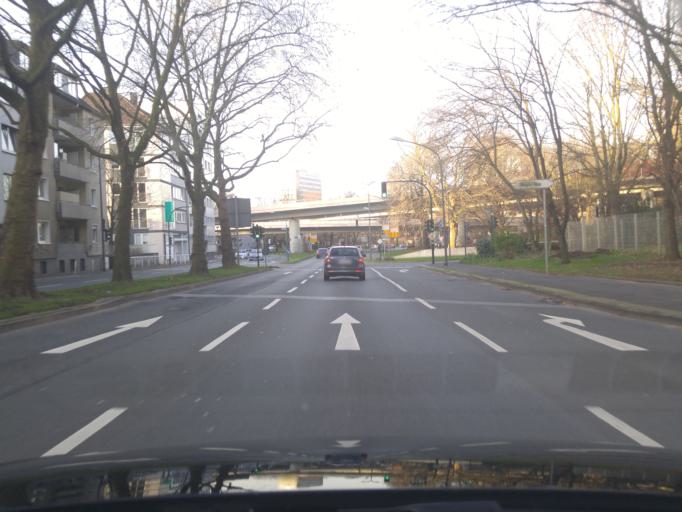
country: DE
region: North Rhine-Westphalia
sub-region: Regierungsbezirk Dusseldorf
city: Essen
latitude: 51.4485
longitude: 7.0191
